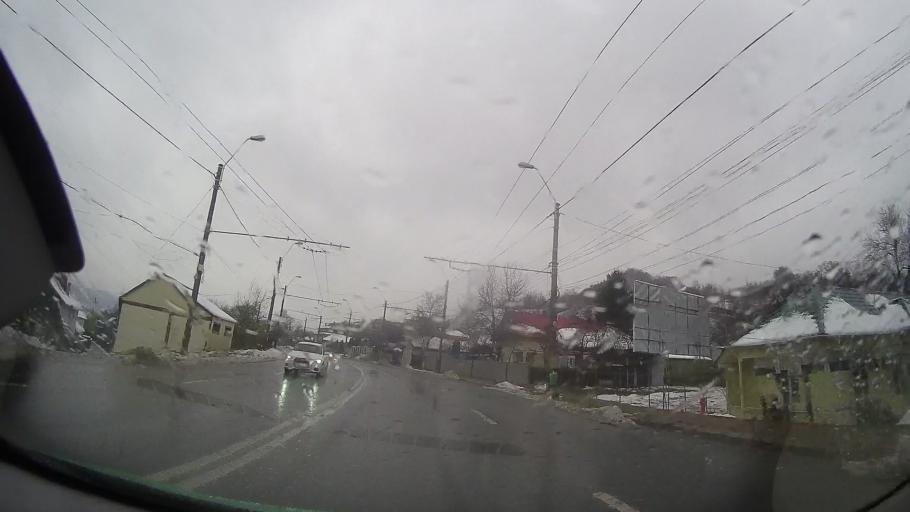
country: RO
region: Neamt
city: Piatra Neamt
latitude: 46.9407
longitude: 26.3284
